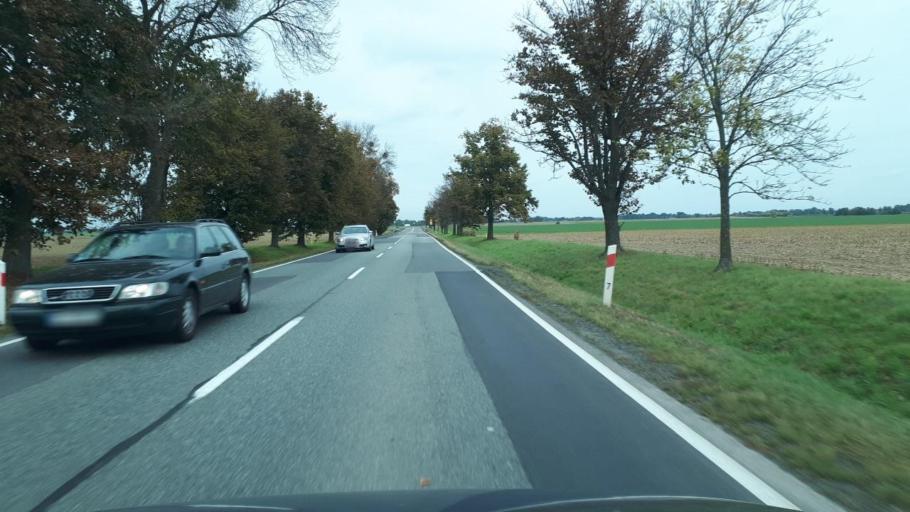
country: PL
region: Opole Voivodeship
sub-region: Powiat kluczborski
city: Byczyna
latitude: 51.0436
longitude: 18.1957
